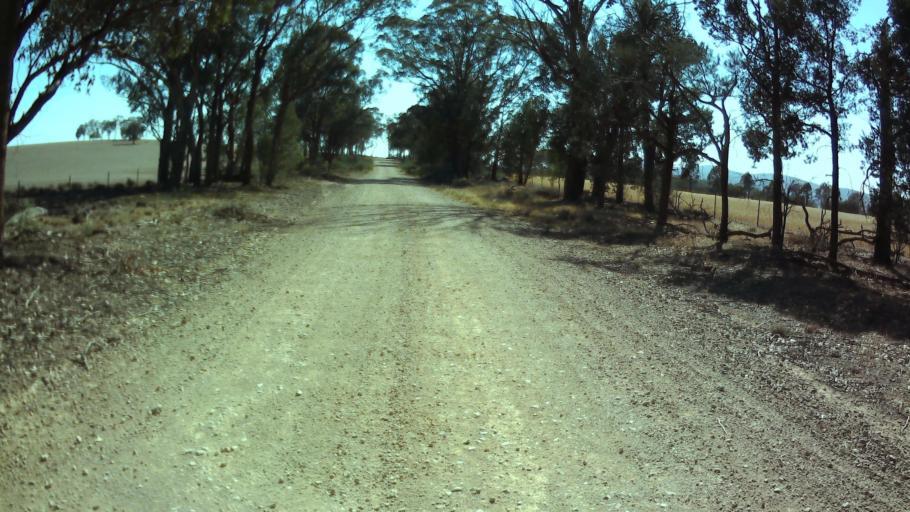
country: AU
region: New South Wales
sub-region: Weddin
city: Grenfell
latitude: -33.9030
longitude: 147.8638
